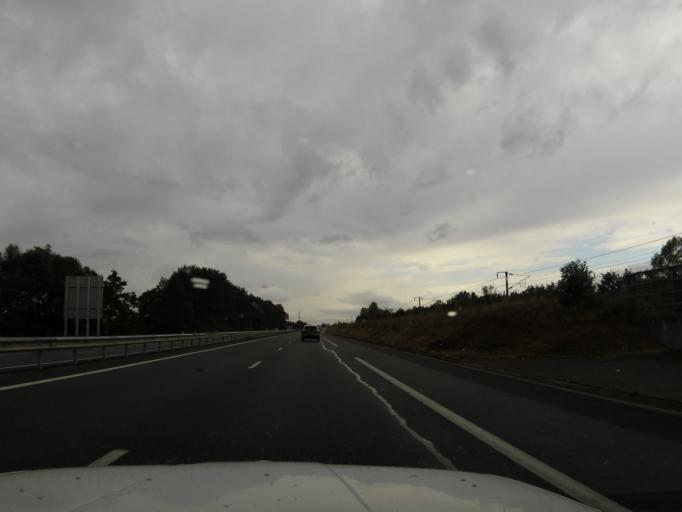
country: FR
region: Rhone-Alpes
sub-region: Departement du Rhone
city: Pusignan
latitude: 45.7773
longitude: 5.0820
